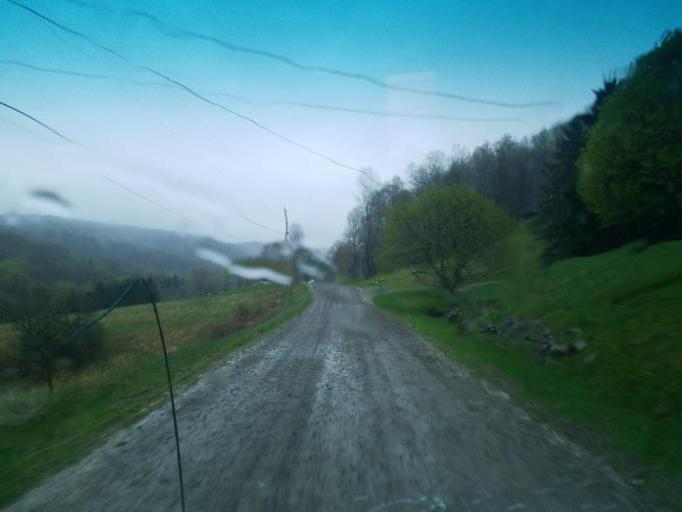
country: US
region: Pennsylvania
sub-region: Tioga County
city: Westfield
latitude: 41.8972
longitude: -77.7108
